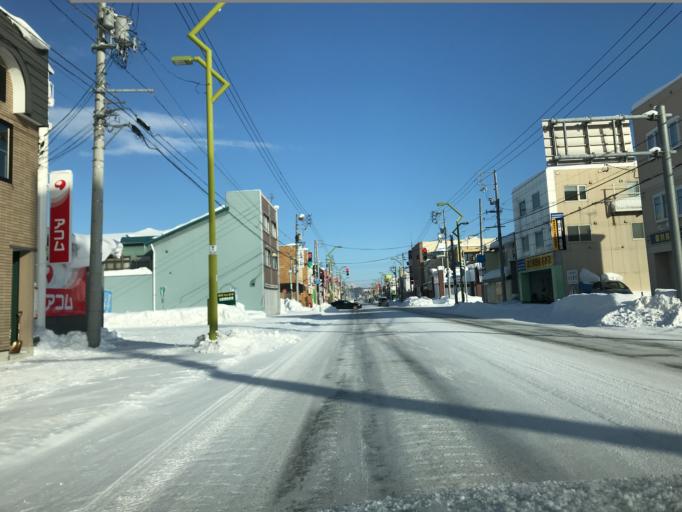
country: JP
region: Hokkaido
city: Nayoro
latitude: 44.3499
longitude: 142.4572
